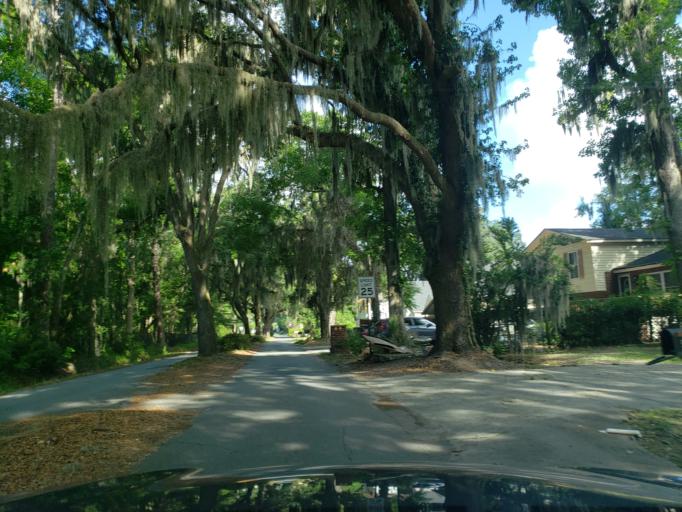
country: US
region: Georgia
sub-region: Chatham County
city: Isle of Hope
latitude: 31.9788
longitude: -81.0632
